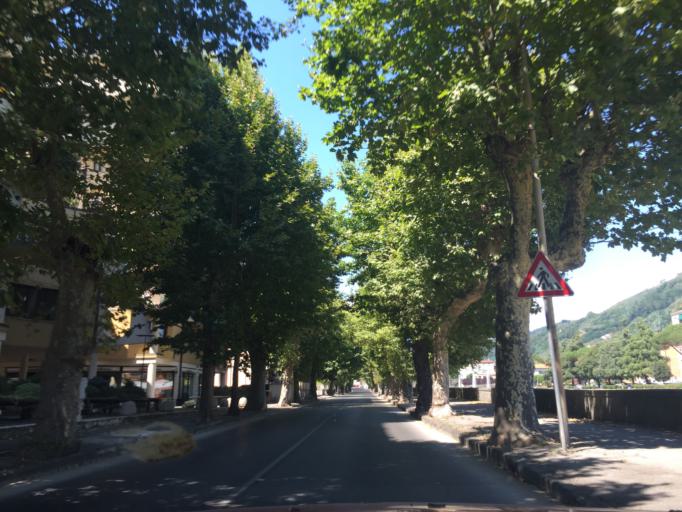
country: IT
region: Tuscany
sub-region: Provincia di Pistoia
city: Pescia
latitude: 43.8977
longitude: 10.6889
